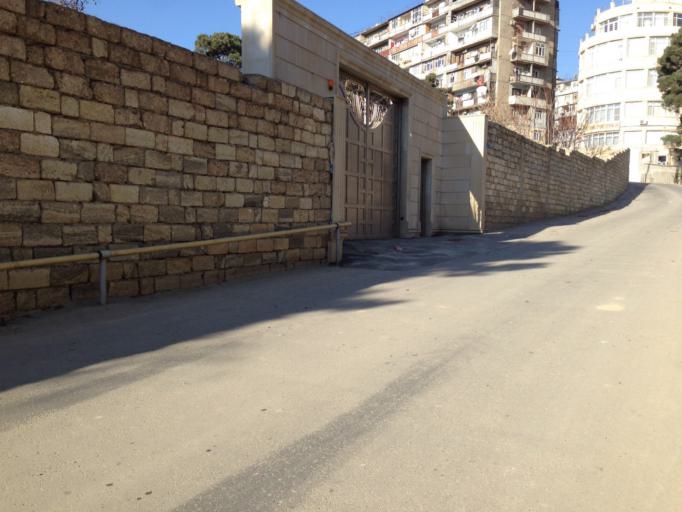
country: AZ
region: Baki
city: Baku
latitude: 40.3906
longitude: 49.8750
